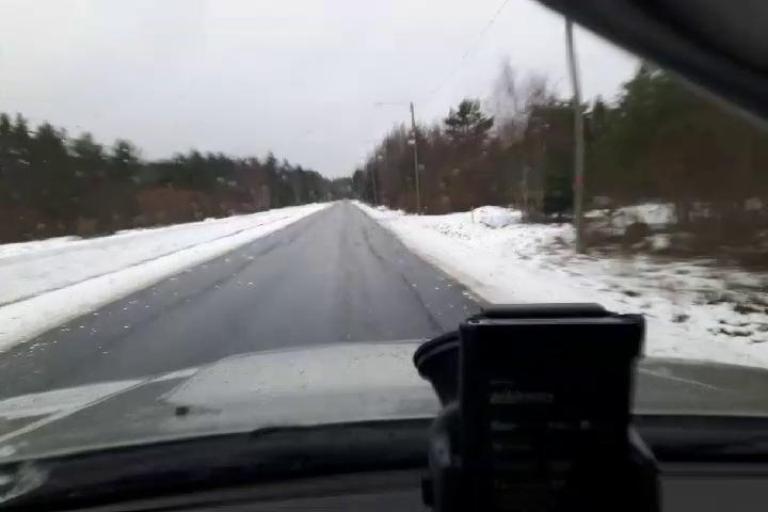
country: EE
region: Harju
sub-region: Harku vald
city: Tabasalu
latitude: 59.4333
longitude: 24.4941
